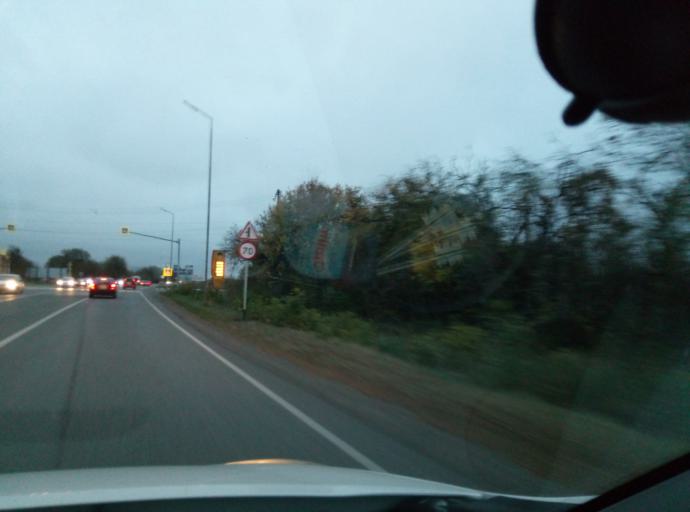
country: RU
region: Stavropol'skiy
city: Vinsady
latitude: 44.0554
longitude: 42.9439
